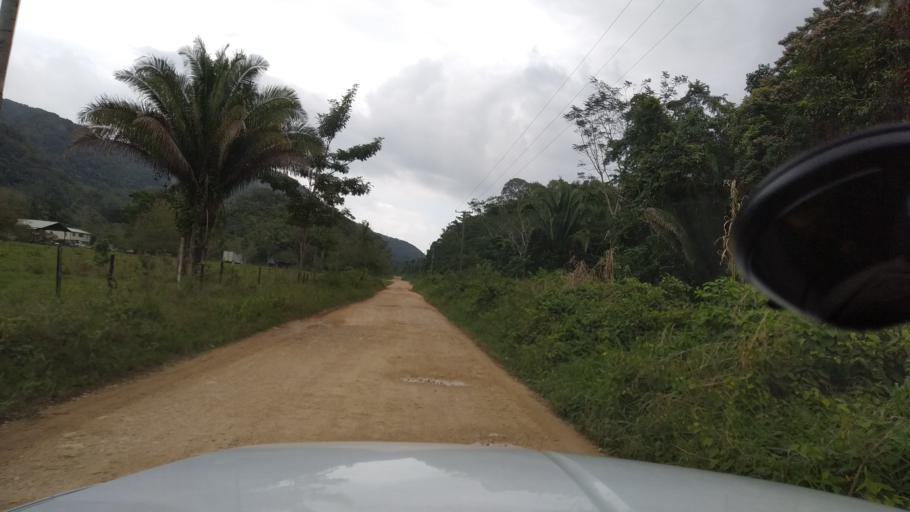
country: BZ
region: Toledo
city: Punta Gorda
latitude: 16.2057
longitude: -89.0298
